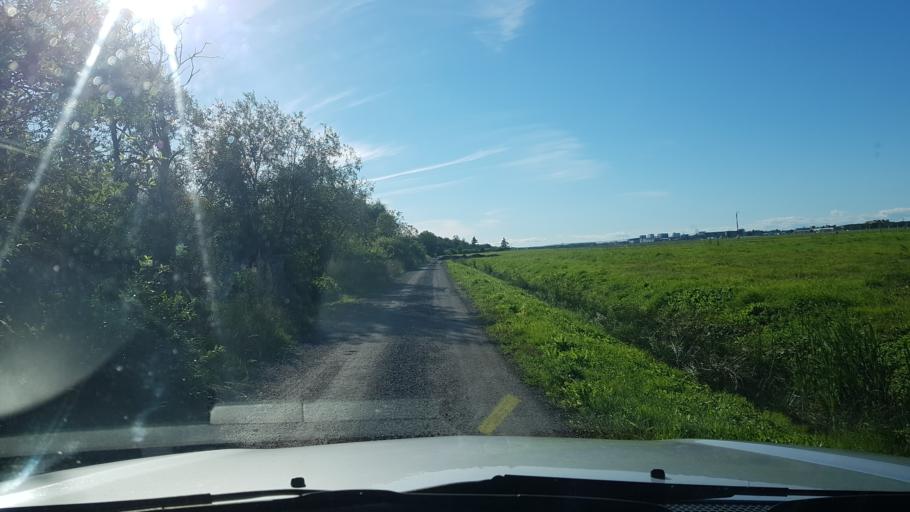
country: EE
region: Harju
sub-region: Tallinna linn
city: Kose
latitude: 59.4093
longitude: 24.8812
